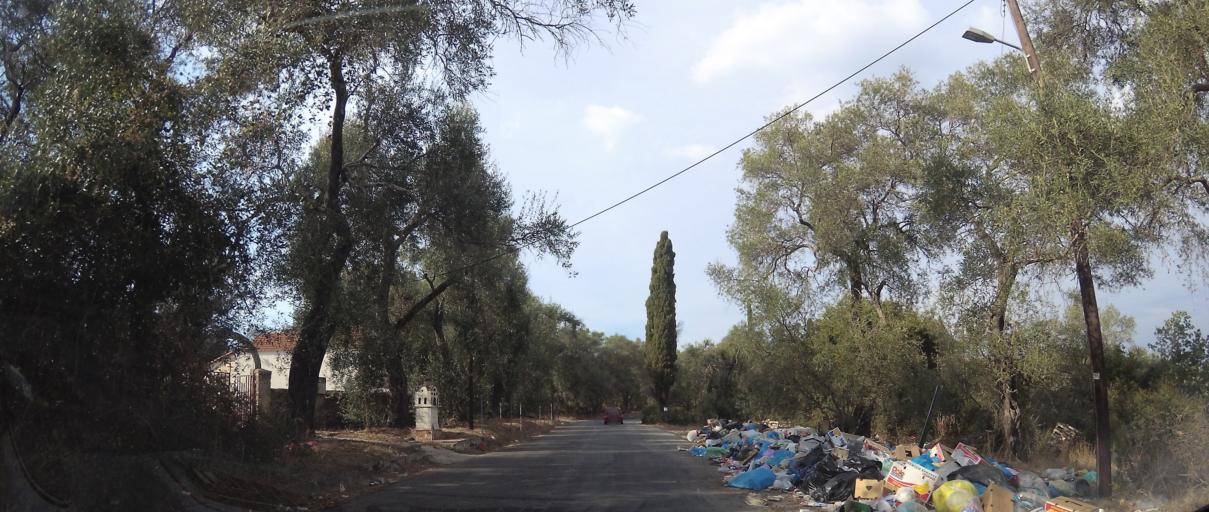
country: GR
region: Ionian Islands
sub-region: Nomos Kerkyras
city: Kynopiastes
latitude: 39.5580
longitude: 19.8616
